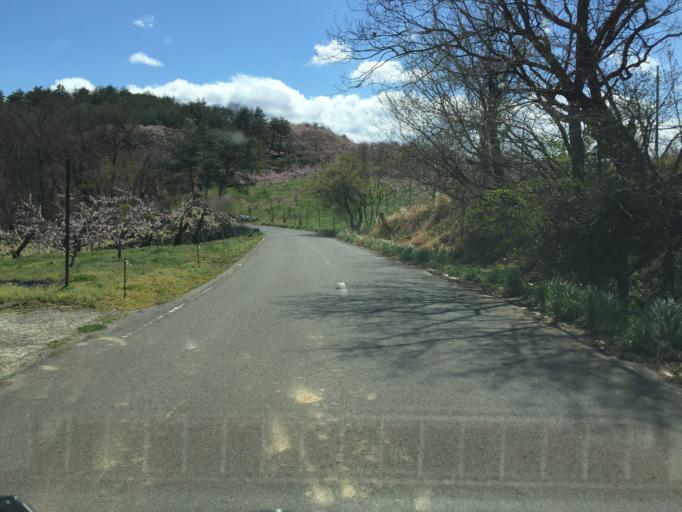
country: JP
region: Fukushima
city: Fukushima-shi
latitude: 37.8319
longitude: 140.4317
